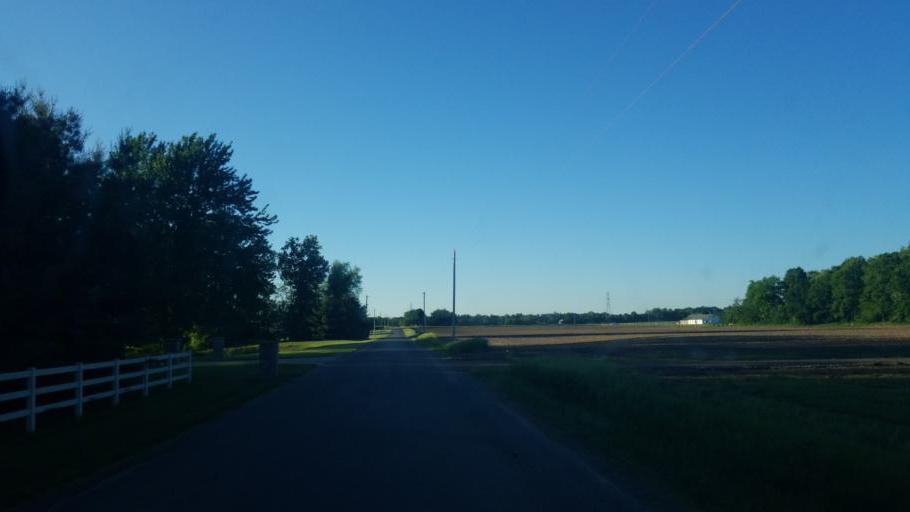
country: US
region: Indiana
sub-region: Elkhart County
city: Nappanee
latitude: 41.4216
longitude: -86.0588
